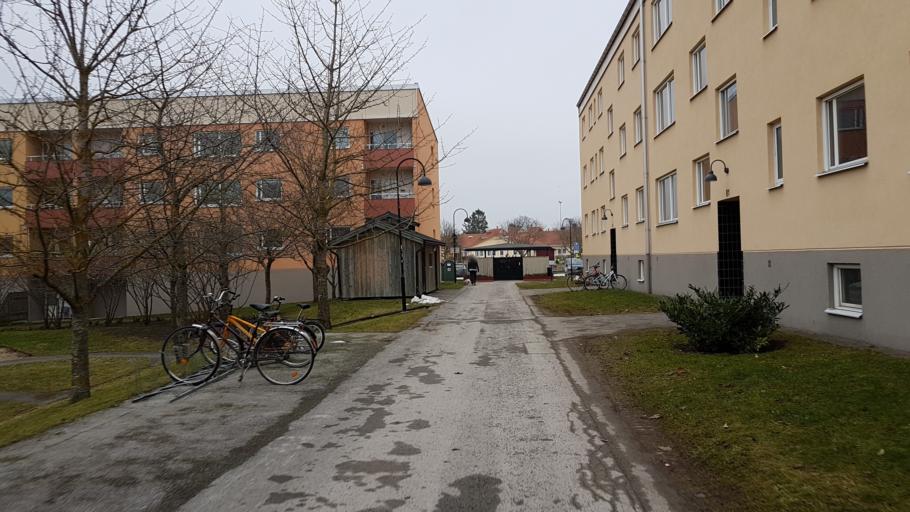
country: SE
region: Gotland
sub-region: Gotland
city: Visby
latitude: 57.6370
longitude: 18.3159
